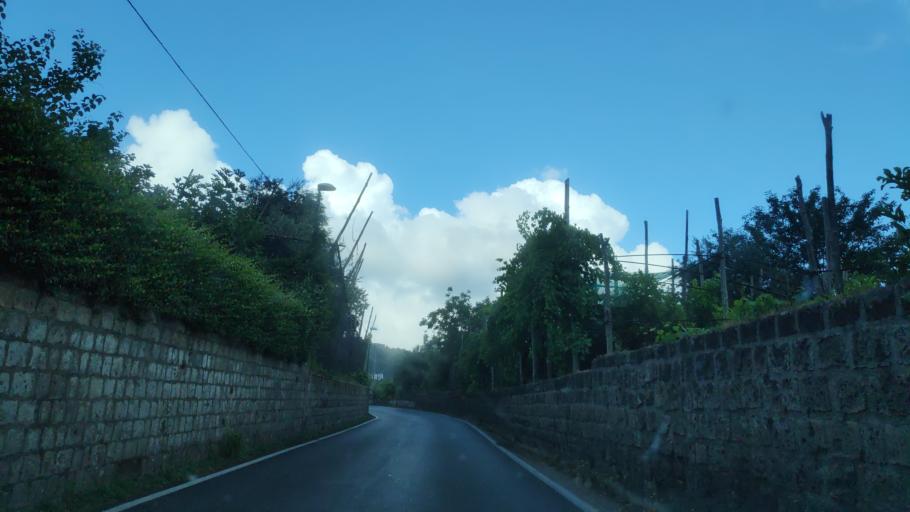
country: IT
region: Campania
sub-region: Provincia di Napoli
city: Piano di Sorrento
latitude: 40.6266
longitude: 14.4244
